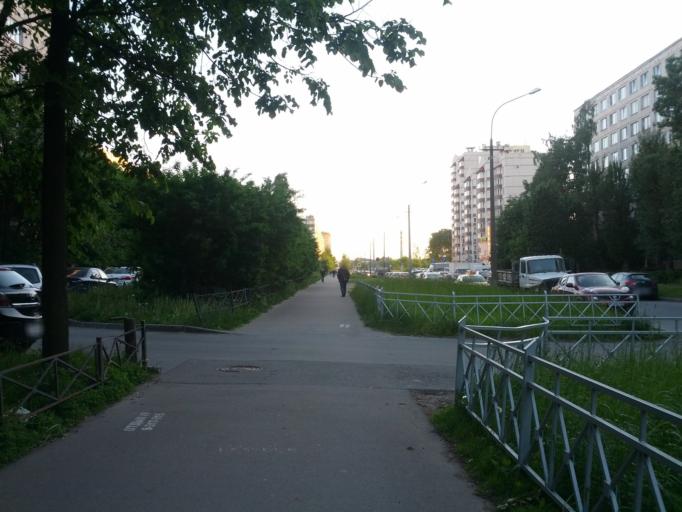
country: RU
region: St.-Petersburg
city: Krasnogvargeisky
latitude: 59.9103
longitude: 30.4753
